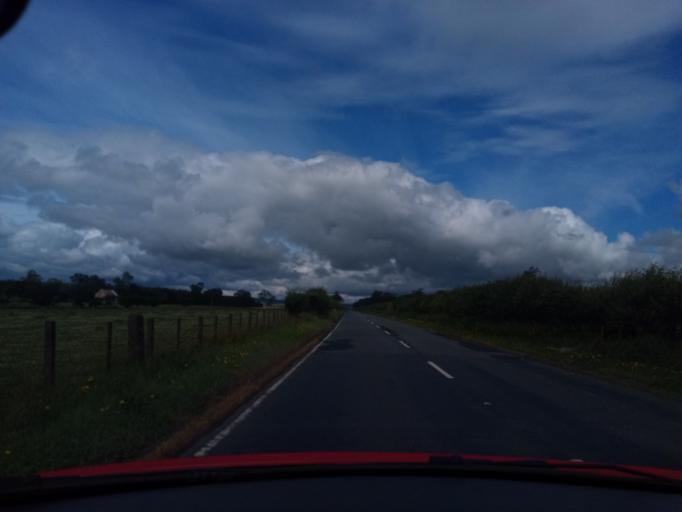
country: GB
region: Scotland
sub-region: The Scottish Borders
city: Lauder
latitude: 55.7293
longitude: -2.7286
